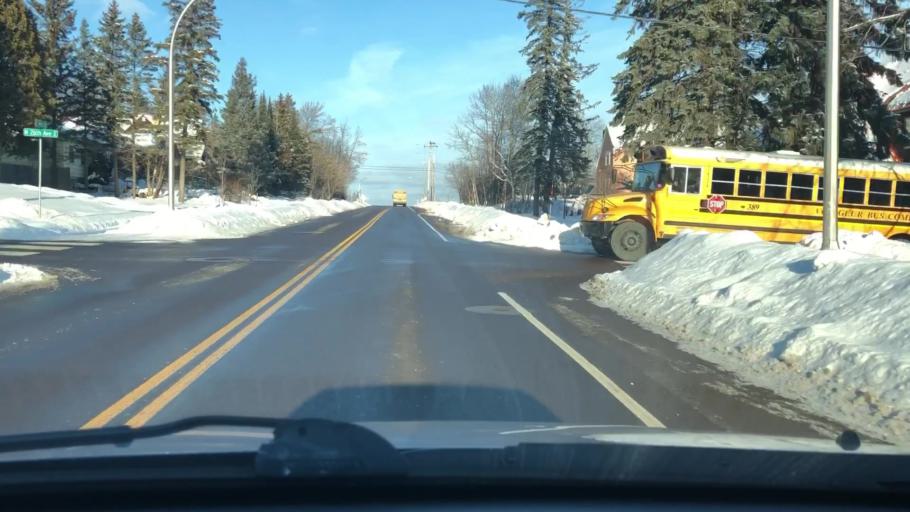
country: US
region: Minnesota
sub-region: Saint Louis County
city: Duluth
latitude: 46.8142
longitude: -92.0705
